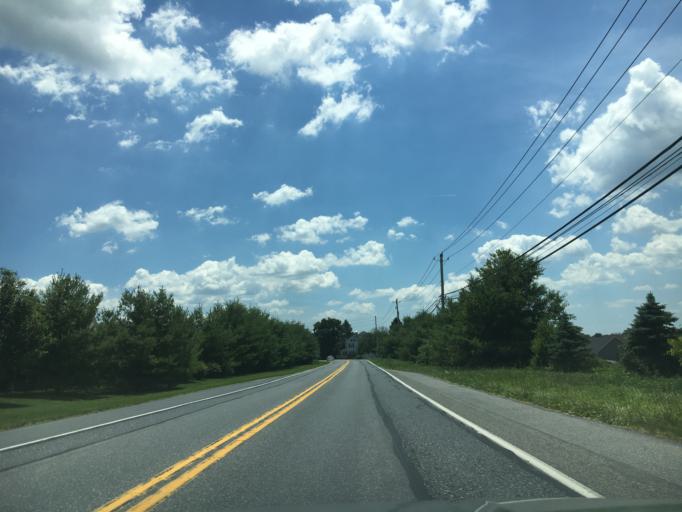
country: US
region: Pennsylvania
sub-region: Lehigh County
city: Schnecksville
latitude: 40.6924
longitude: -75.5904
